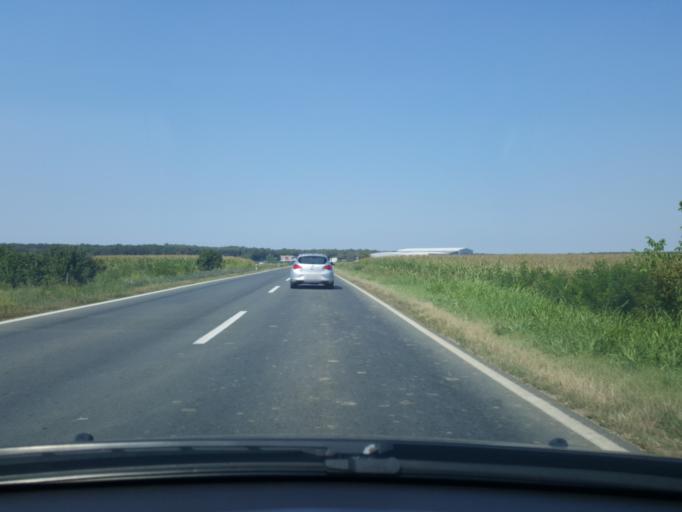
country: RS
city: Klenak
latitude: 44.7928
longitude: 19.7262
